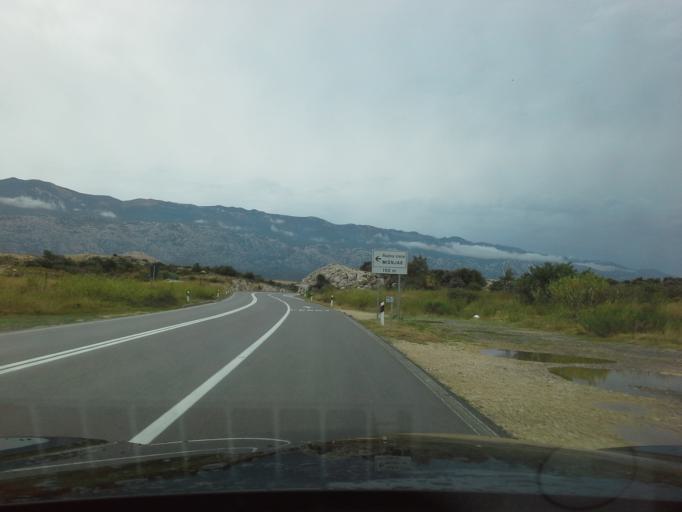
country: HR
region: Primorsko-Goranska
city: Banjol
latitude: 44.7060
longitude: 14.8409
